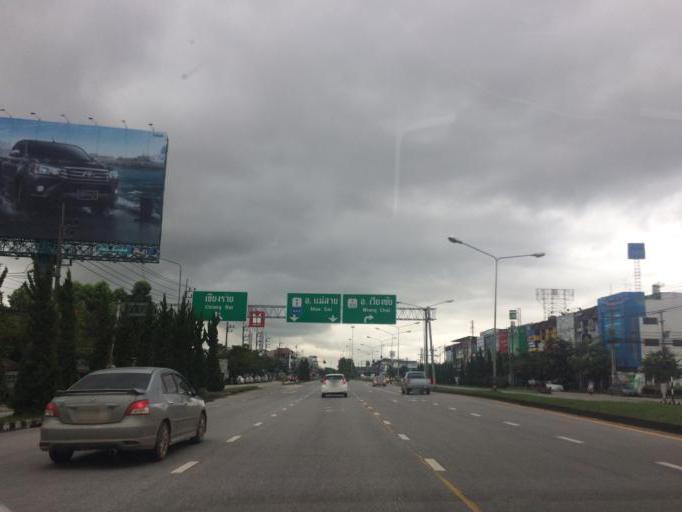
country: TH
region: Chiang Rai
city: Chiang Rai
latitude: 19.8961
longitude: 99.8383
